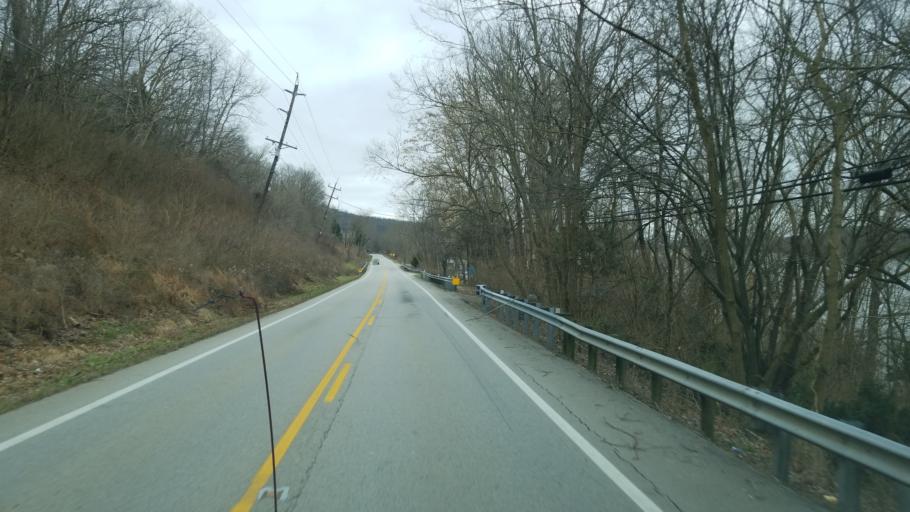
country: US
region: Ohio
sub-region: Clermont County
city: New Richmond
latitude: 38.9010
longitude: -84.2391
